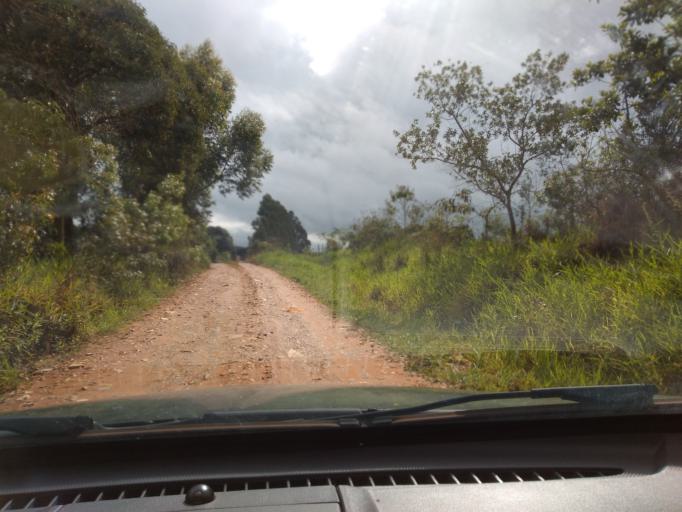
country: BR
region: Minas Gerais
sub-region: Lavras
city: Lavras
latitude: -21.5071
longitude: -44.9195
